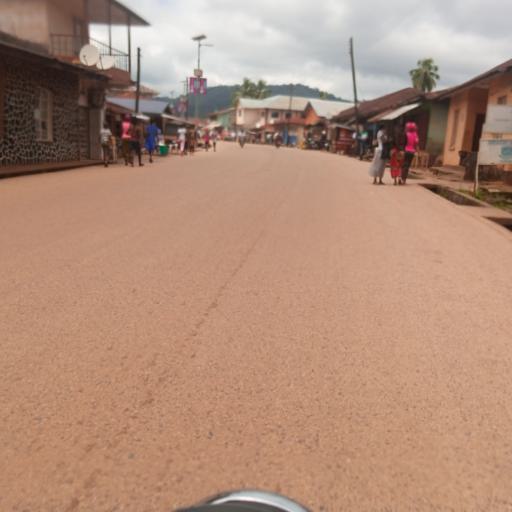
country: SL
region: Eastern Province
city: Kenema
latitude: 7.8768
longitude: -11.1876
